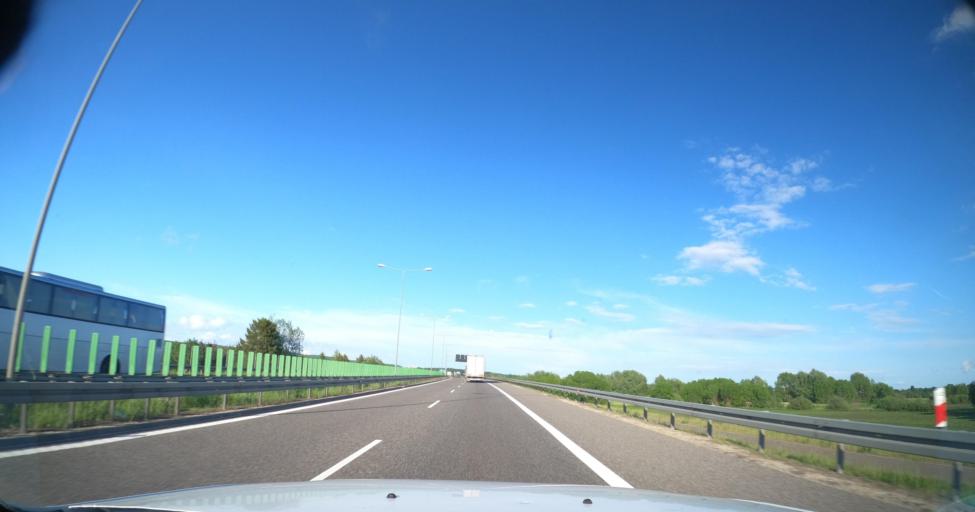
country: PL
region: Warmian-Masurian Voivodeship
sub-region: Powiat elblaski
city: Gronowo Gorne
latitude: 54.1363
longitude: 19.4358
